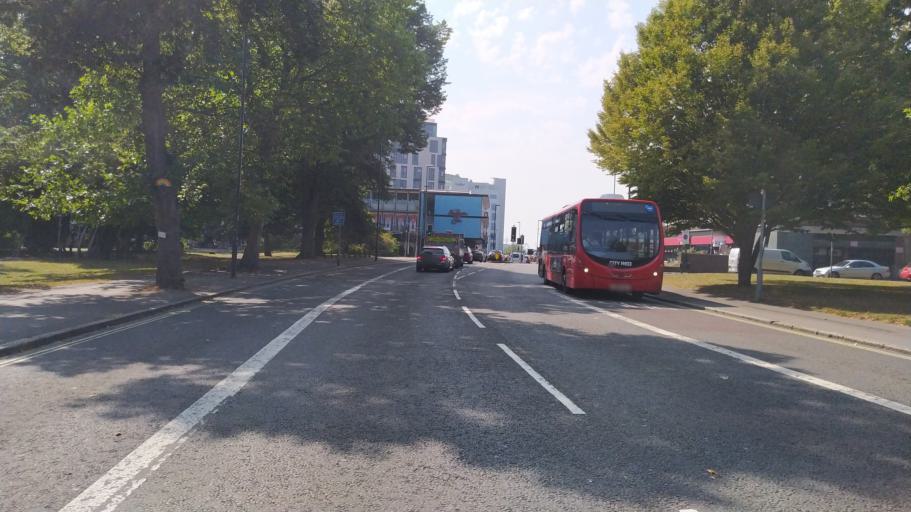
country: GB
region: England
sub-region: Southampton
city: Southampton
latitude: 50.9069
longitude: -1.4032
